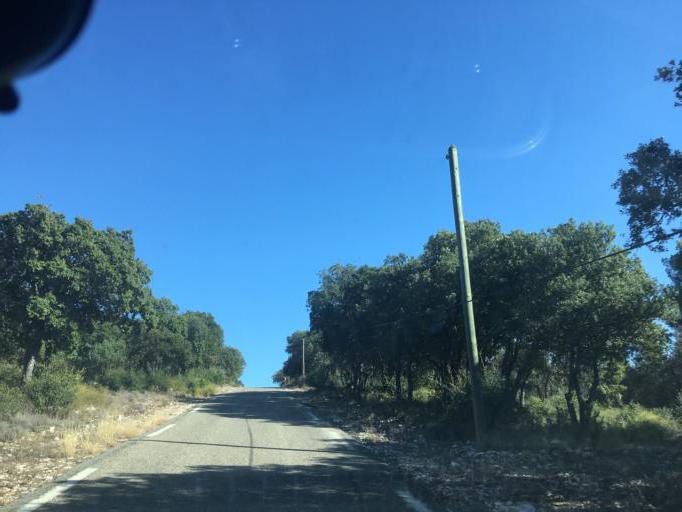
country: FR
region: Provence-Alpes-Cote d'Azur
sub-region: Departement du Var
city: Regusse
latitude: 43.7276
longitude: 6.1201
